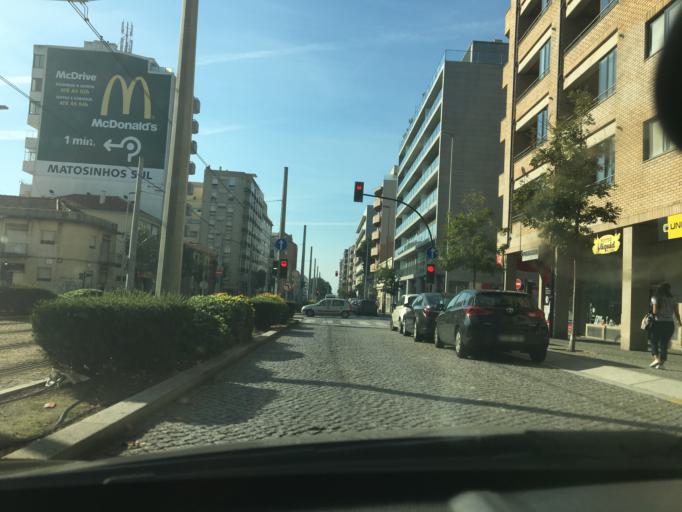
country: PT
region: Porto
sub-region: Matosinhos
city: Matosinhos
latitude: 41.1804
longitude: -8.6861
